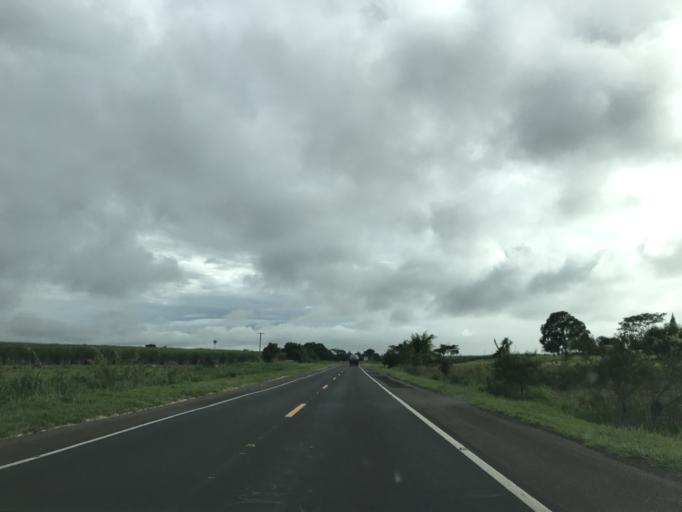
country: BR
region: Sao Paulo
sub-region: Penapolis
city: Penapolis
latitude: -21.4674
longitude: -50.1841
